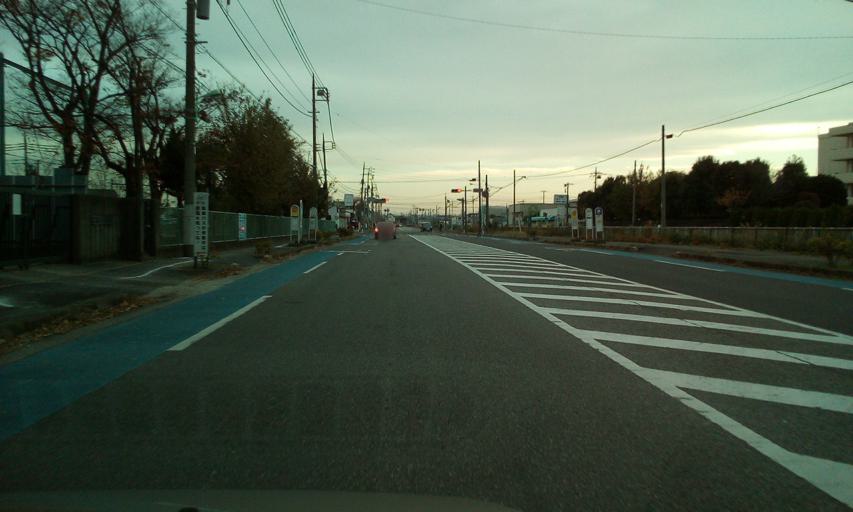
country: JP
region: Saitama
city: Yashio-shi
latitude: 35.8530
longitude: 139.8602
